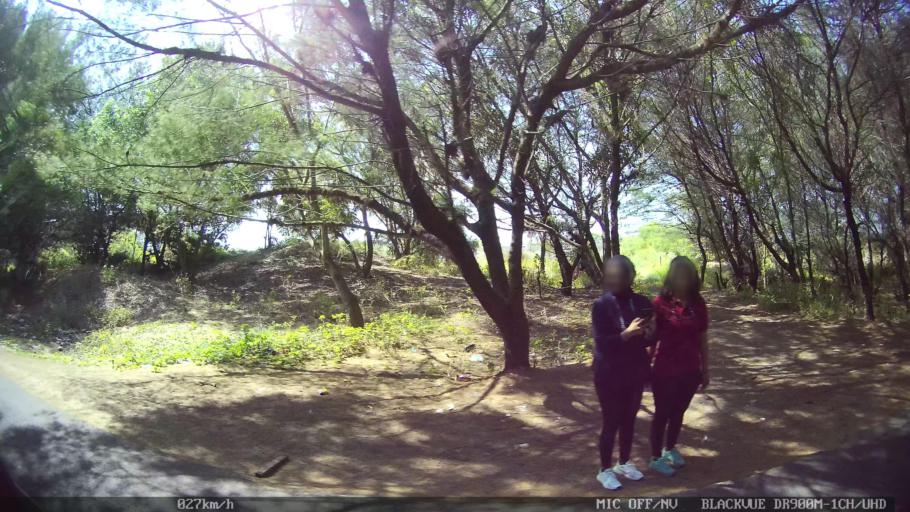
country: ID
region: Daerah Istimewa Yogyakarta
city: Bambanglipuro
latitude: -8.0164
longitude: 110.3049
